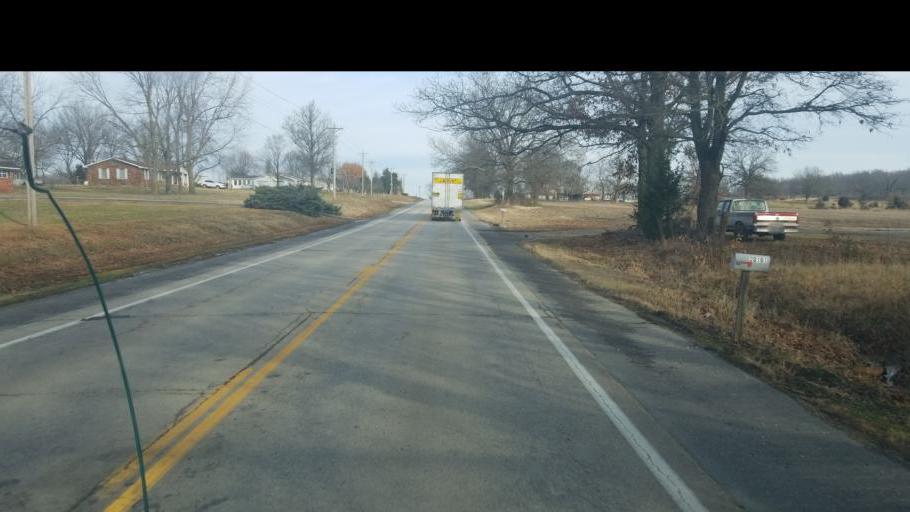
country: US
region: Missouri
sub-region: Stoddard County
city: Bloomfield
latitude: 36.9056
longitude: -89.9224
